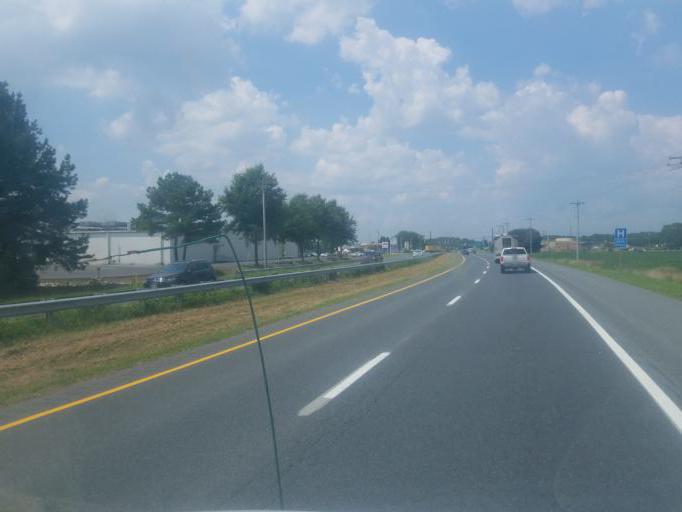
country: US
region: Maryland
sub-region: Worcester County
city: Berlin
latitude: 38.3327
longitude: -75.2099
